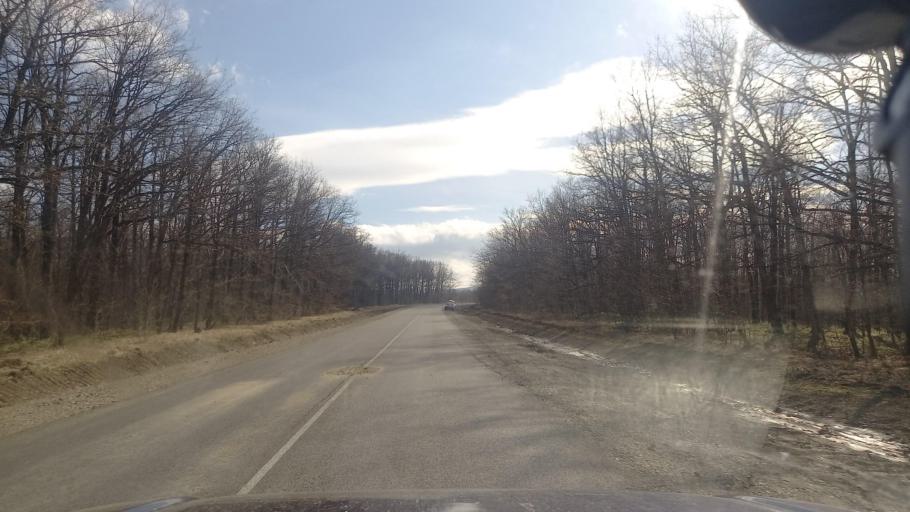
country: RU
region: Krasnodarskiy
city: Novodmitriyevskaya
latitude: 44.7377
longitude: 38.9958
